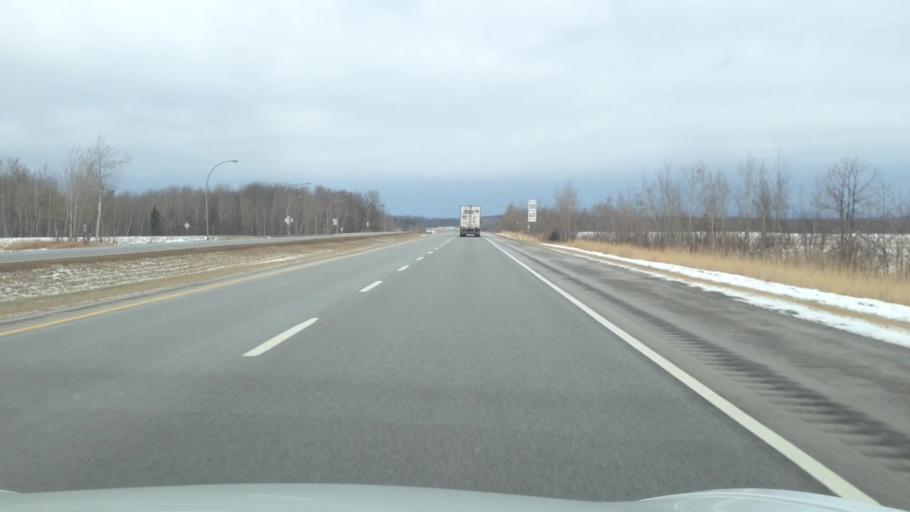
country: CA
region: Quebec
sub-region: Monteregie
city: Rigaud
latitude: 45.5202
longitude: -74.3760
